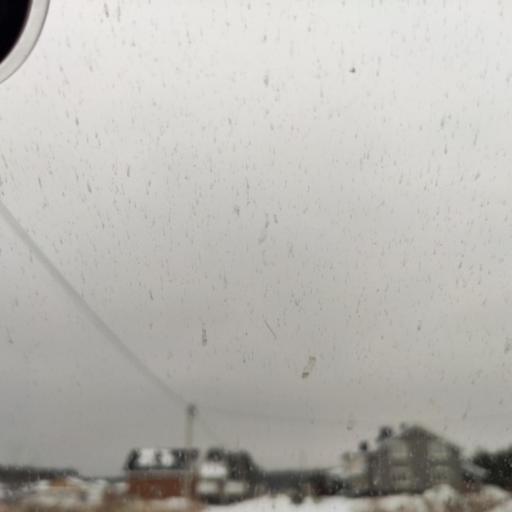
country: RU
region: Voronezj
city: Podgornoye
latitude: 51.8543
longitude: 39.1904
